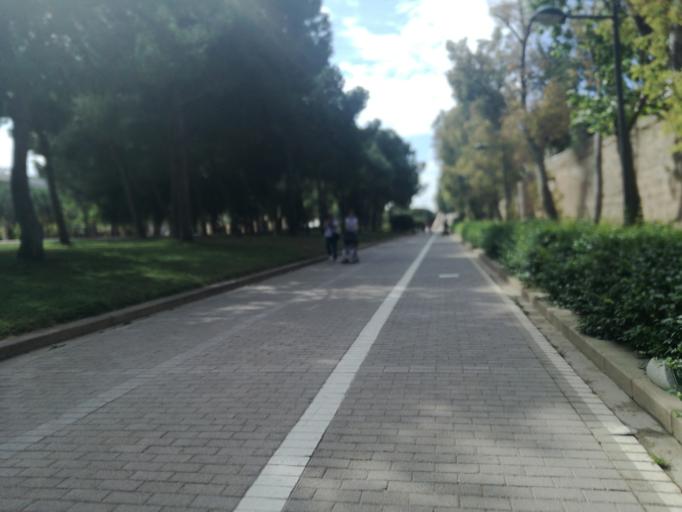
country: ES
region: Valencia
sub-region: Provincia de Valencia
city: Valencia
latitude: 39.4674
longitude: -0.3629
